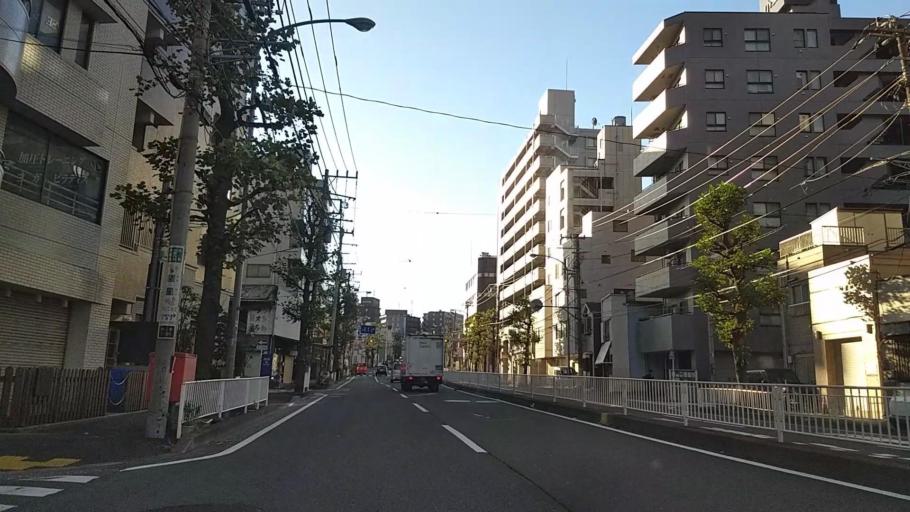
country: JP
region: Kanagawa
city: Yokohama
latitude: 35.4561
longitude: 139.6186
